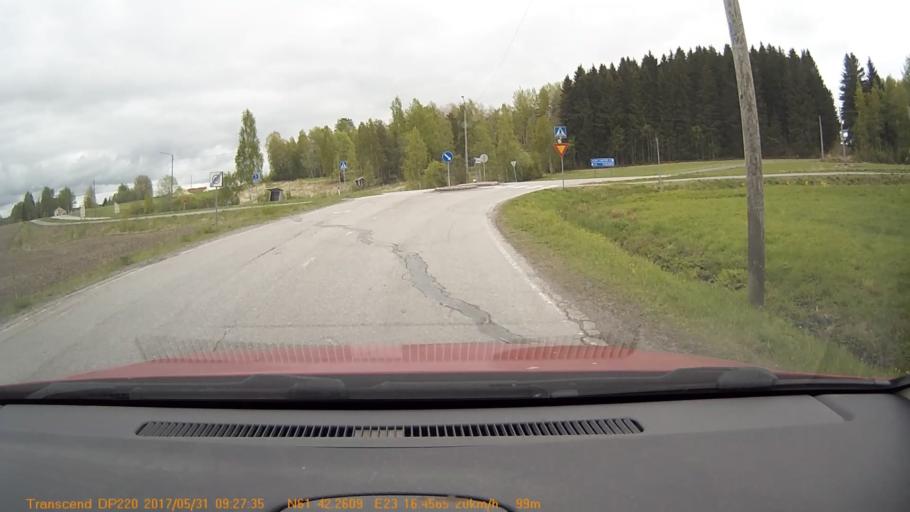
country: FI
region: Pirkanmaa
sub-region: Tampere
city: Viljakkala
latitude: 61.7044
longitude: 23.2747
